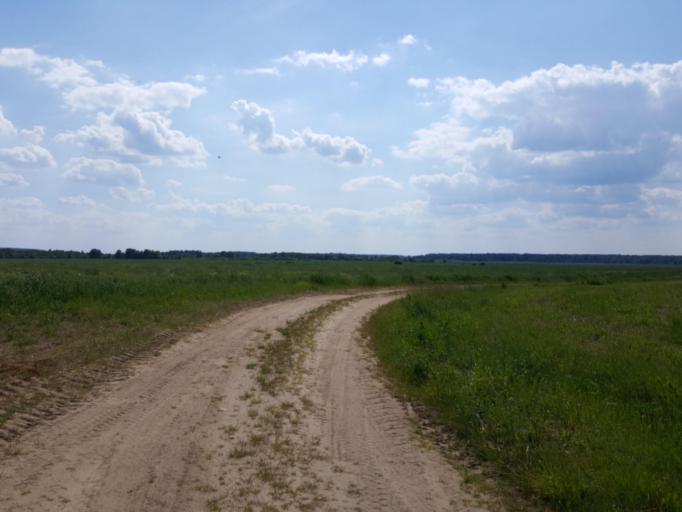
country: BY
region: Brest
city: Kamyanyuki
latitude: 52.4743
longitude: 23.6005
